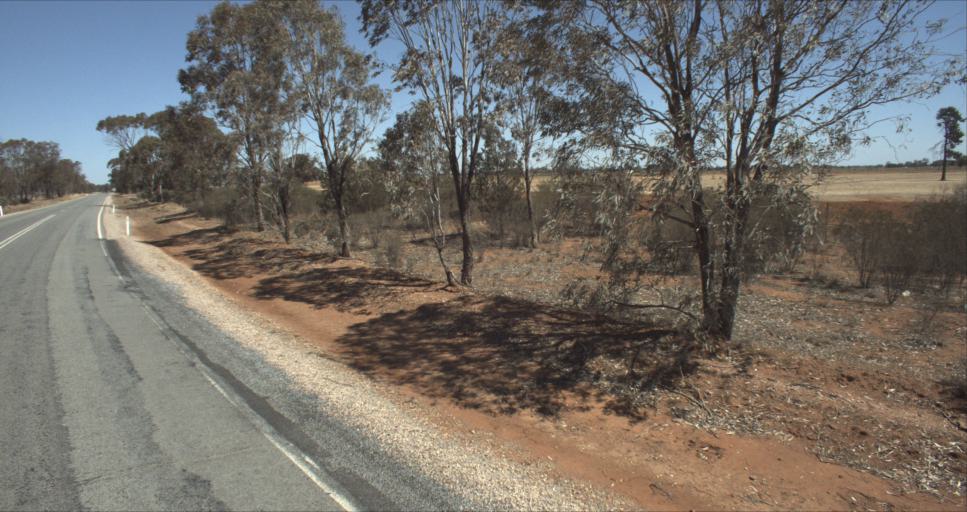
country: AU
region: New South Wales
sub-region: Leeton
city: Leeton
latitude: -34.4969
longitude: 146.4334
